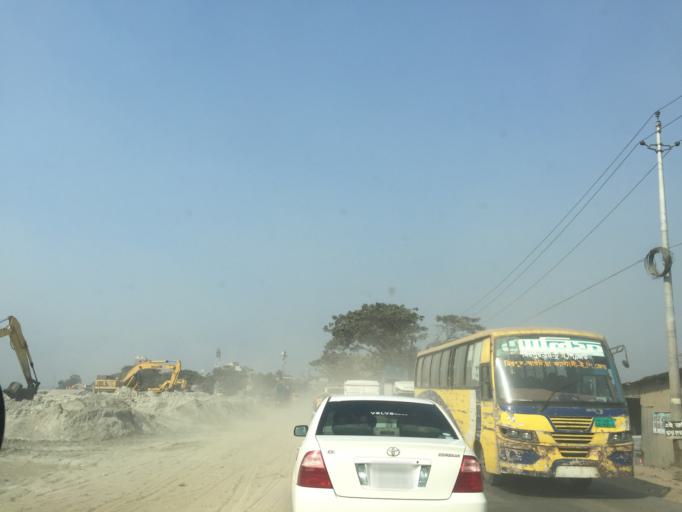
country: BD
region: Dhaka
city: Azimpur
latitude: 23.8042
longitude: 90.3435
